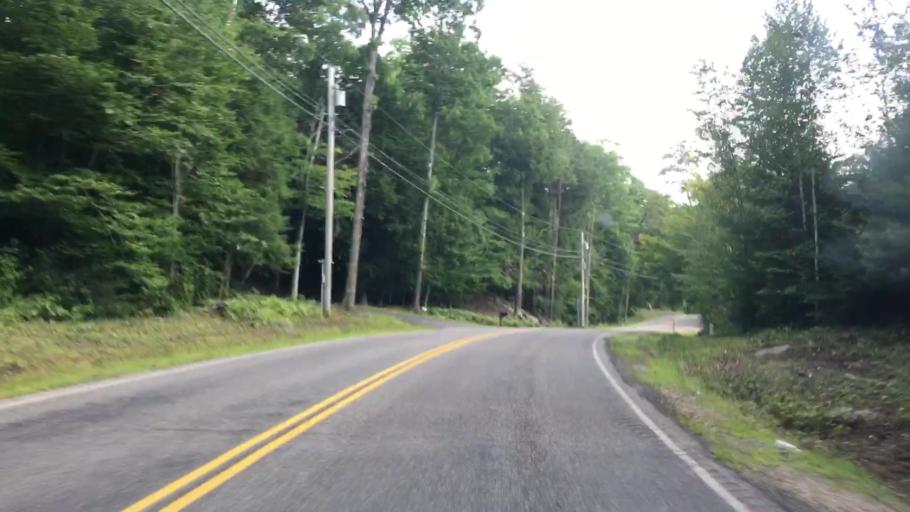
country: US
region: New Hampshire
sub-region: Belknap County
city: Sanbornton
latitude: 43.4963
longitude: -71.5911
